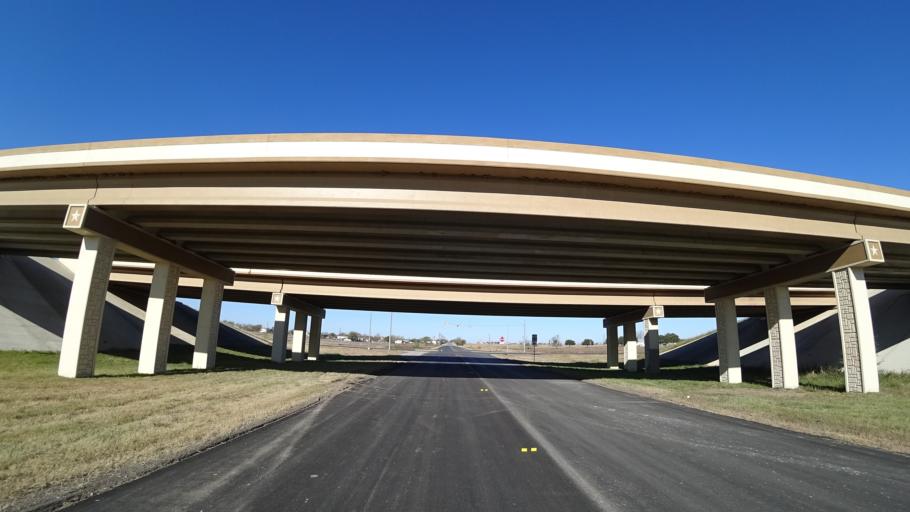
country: US
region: Texas
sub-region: Travis County
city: Onion Creek
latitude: 30.0925
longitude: -97.6790
